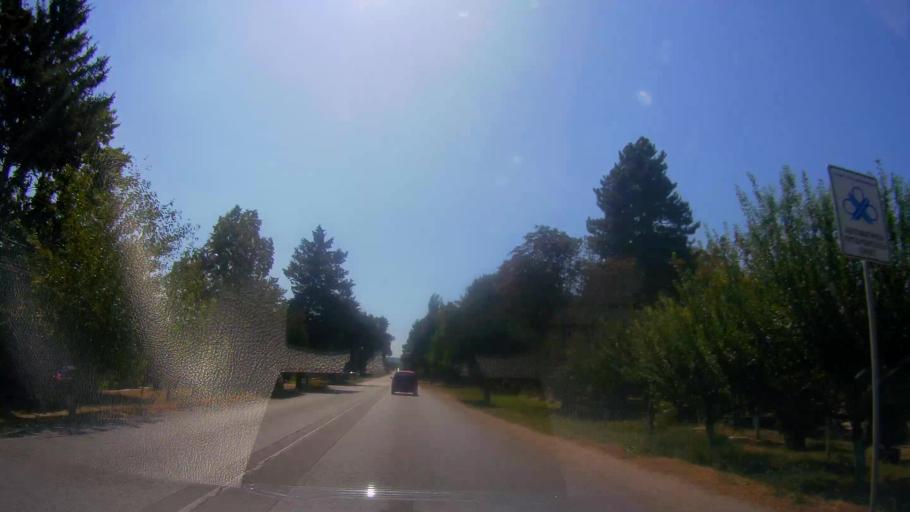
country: BG
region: Veliko Turnovo
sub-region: Obshtina Gorna Oryakhovitsa
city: Purvomaytsi
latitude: 43.1813
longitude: 25.6194
